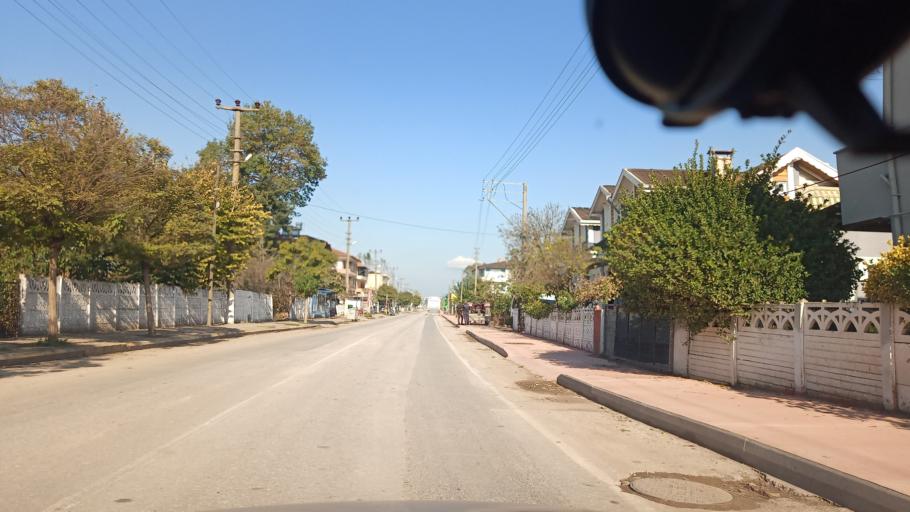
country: TR
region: Sakarya
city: Sogutlu
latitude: 40.9097
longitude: 30.4738
